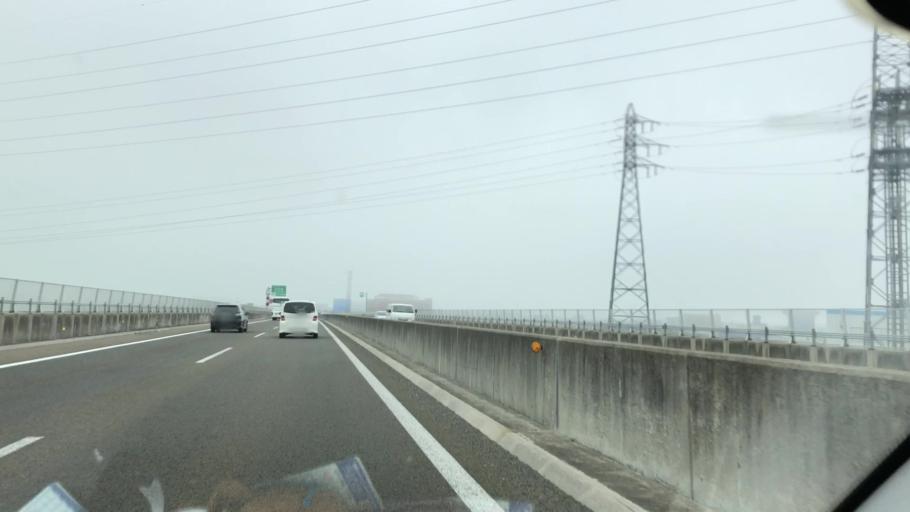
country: JP
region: Miyagi
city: Rifu
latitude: 38.2509
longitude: 140.9573
